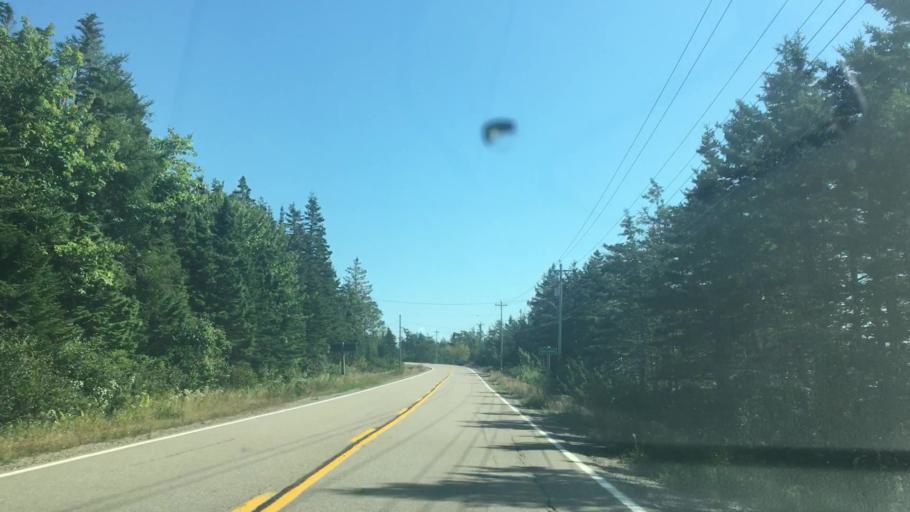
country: CA
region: Nova Scotia
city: Antigonish
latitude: 45.0217
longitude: -62.0098
